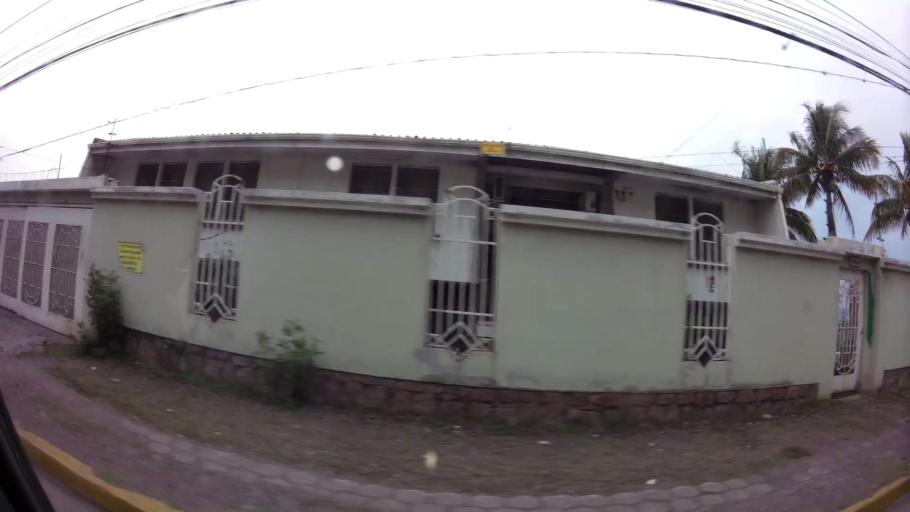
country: HN
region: Francisco Morazan
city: Tegucigalpa
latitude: 14.0812
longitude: -87.2012
